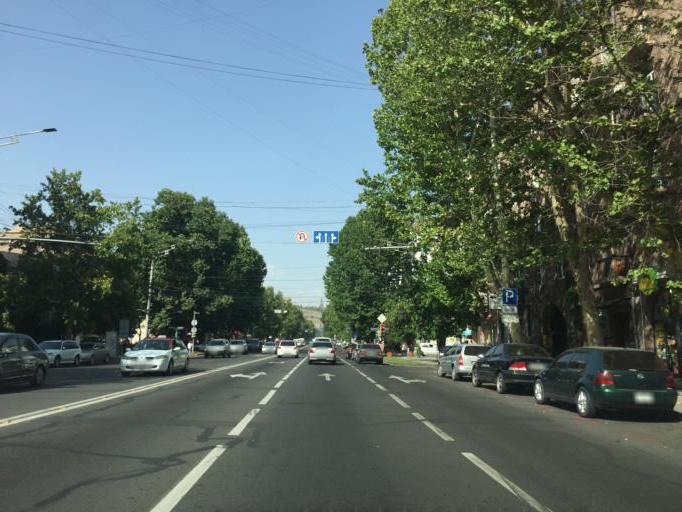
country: AM
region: Yerevan
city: Yerevan
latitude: 40.1788
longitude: 44.5052
